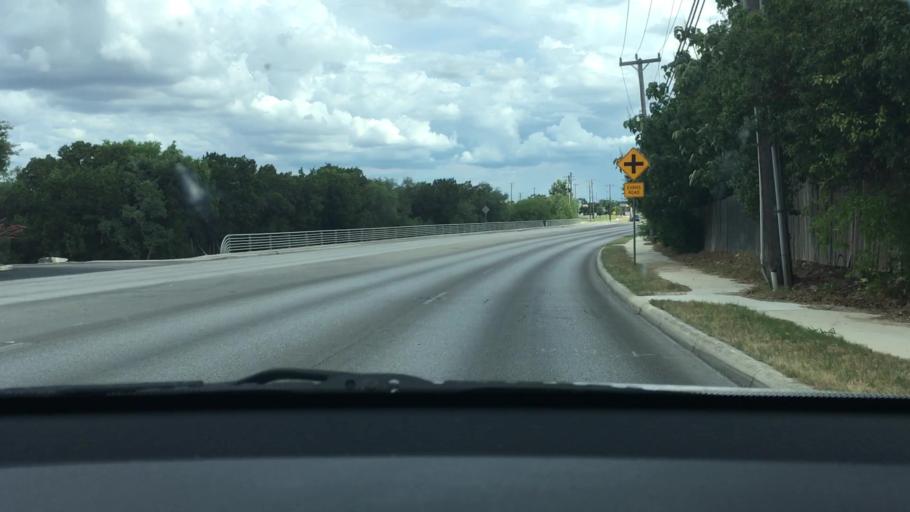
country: US
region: Texas
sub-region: Bexar County
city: Timberwood Park
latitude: 29.6513
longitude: -98.4261
